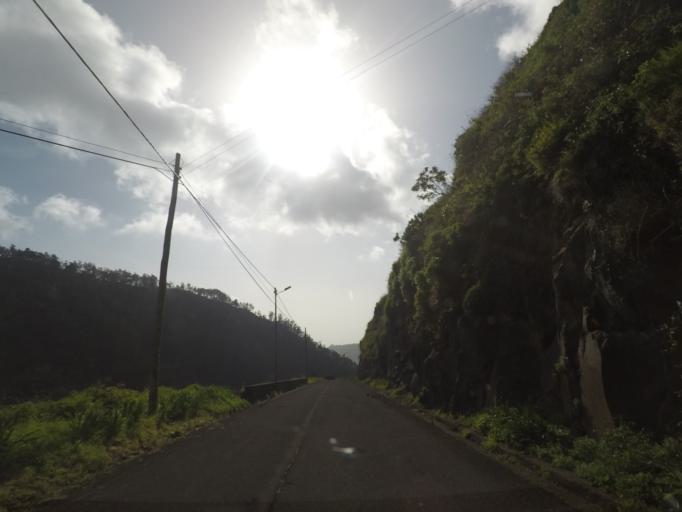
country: PT
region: Madeira
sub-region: Ribeira Brava
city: Campanario
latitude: 32.7039
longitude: -17.0266
